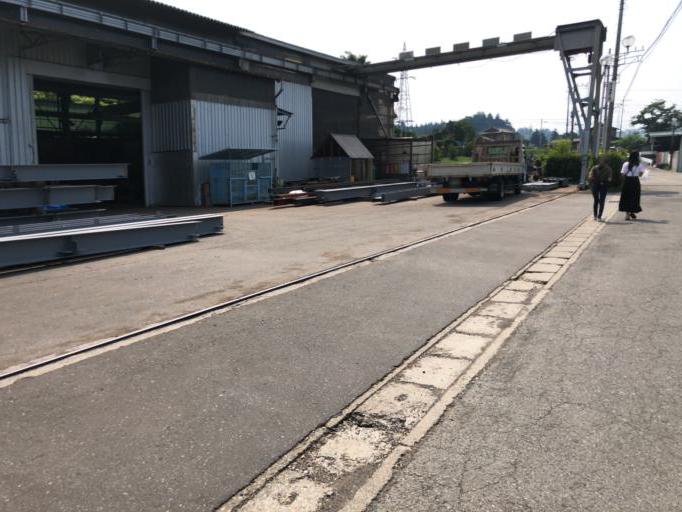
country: JP
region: Saitama
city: Chichibu
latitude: 35.9836
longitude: 139.1043
